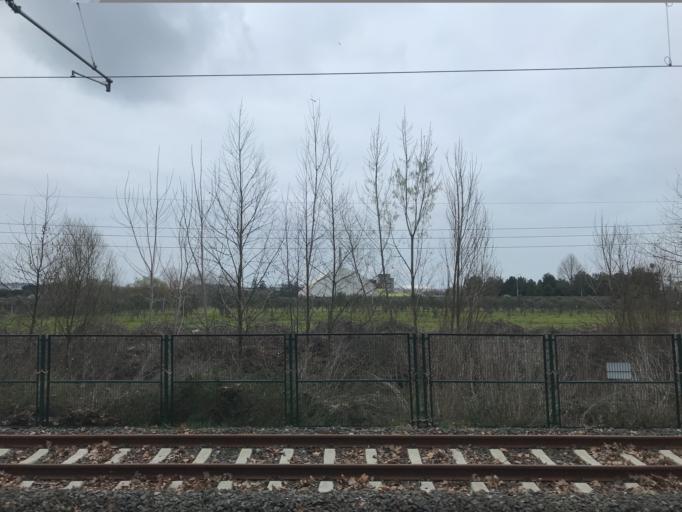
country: TR
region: Kocaeli
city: Darica
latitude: 40.8099
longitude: 29.3518
